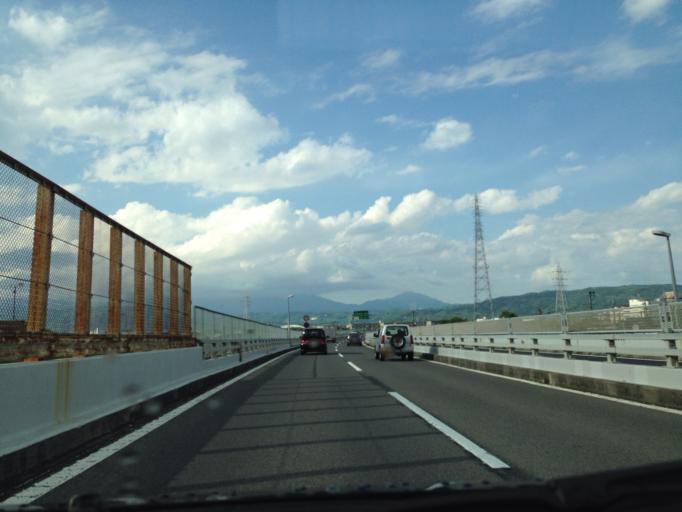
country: JP
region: Kanagawa
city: Odawara
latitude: 35.2782
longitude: 139.1513
